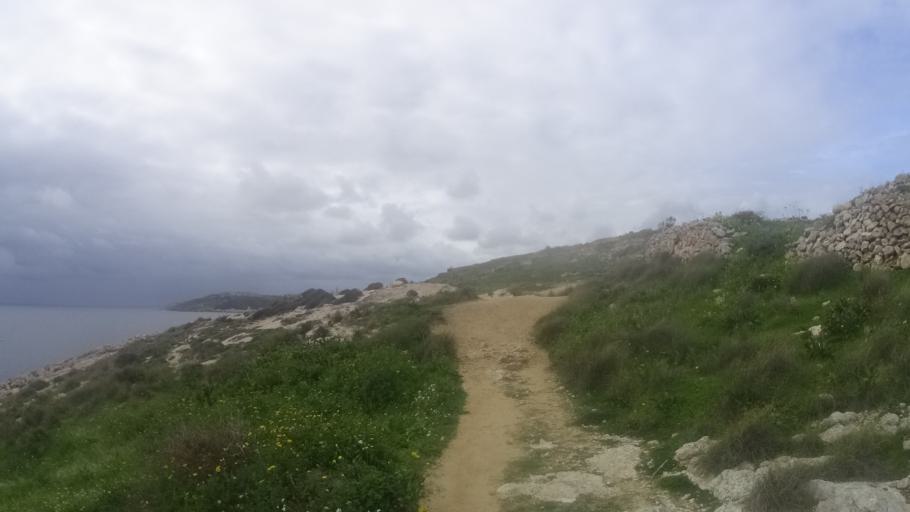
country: MT
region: Il-Qala
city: Qala
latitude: 36.0263
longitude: 14.3187
